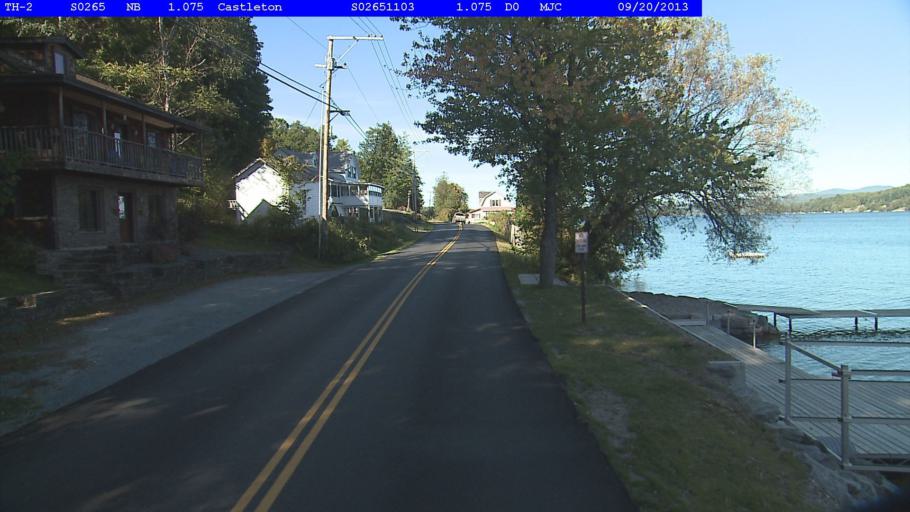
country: US
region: Vermont
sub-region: Rutland County
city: Fair Haven
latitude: 43.6194
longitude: -73.2302
